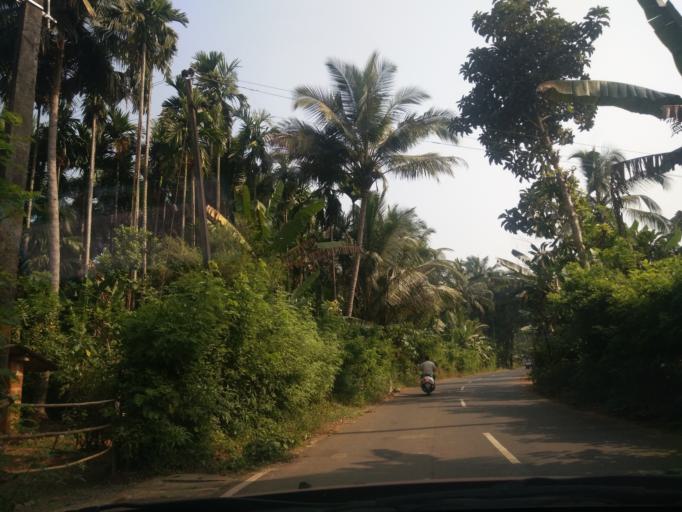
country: IN
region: Goa
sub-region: North Goa
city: Palle
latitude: 15.4813
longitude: 74.1267
